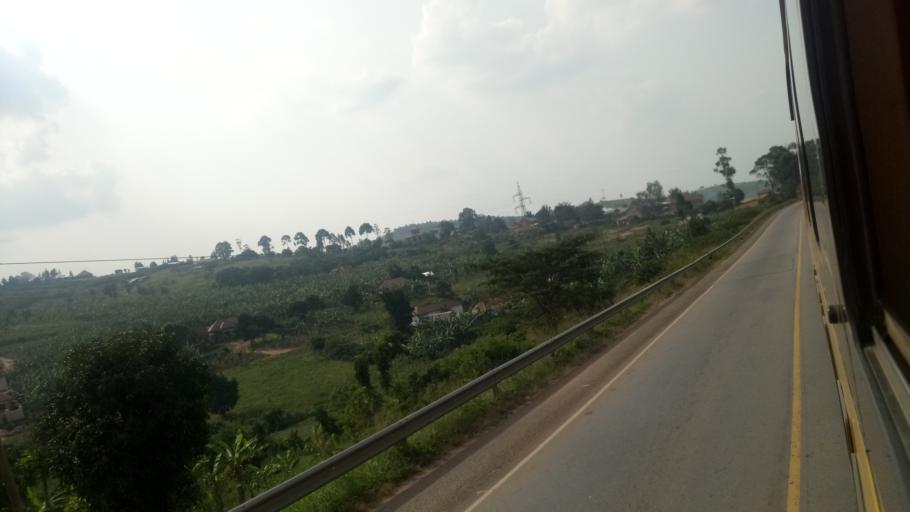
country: UG
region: Western Region
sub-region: Mbarara District
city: Mbarara
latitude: -0.5354
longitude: 30.7155
